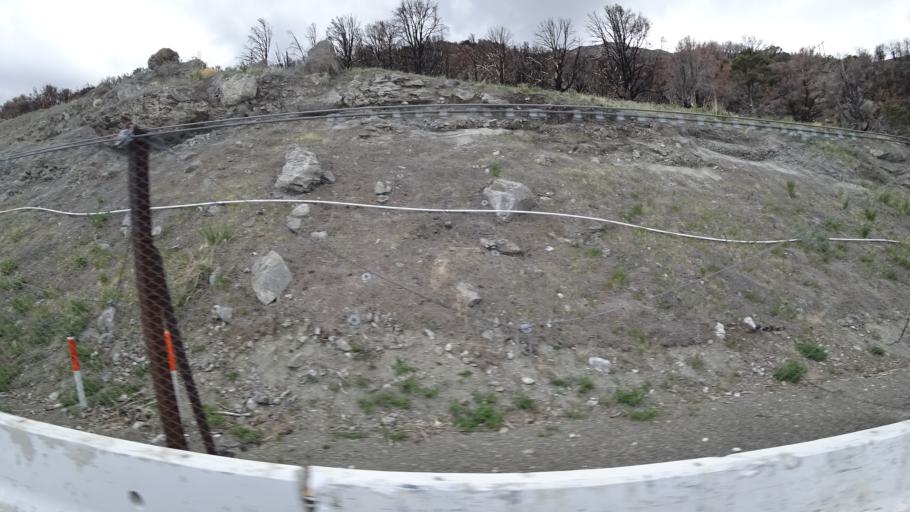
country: US
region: California
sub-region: Mono County
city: Bridgeport
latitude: 37.9790
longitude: -119.1374
